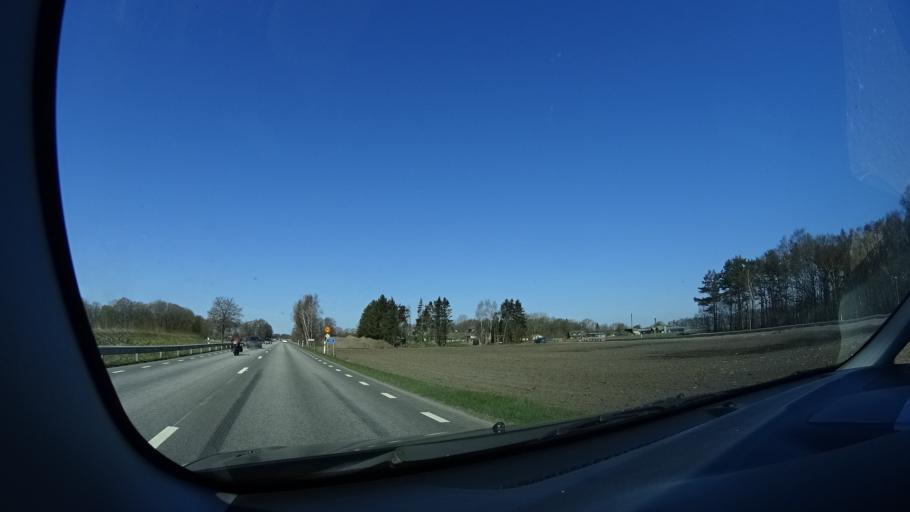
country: SE
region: Skane
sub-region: Helsingborg
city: Odakra
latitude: 56.2117
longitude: 12.6977
